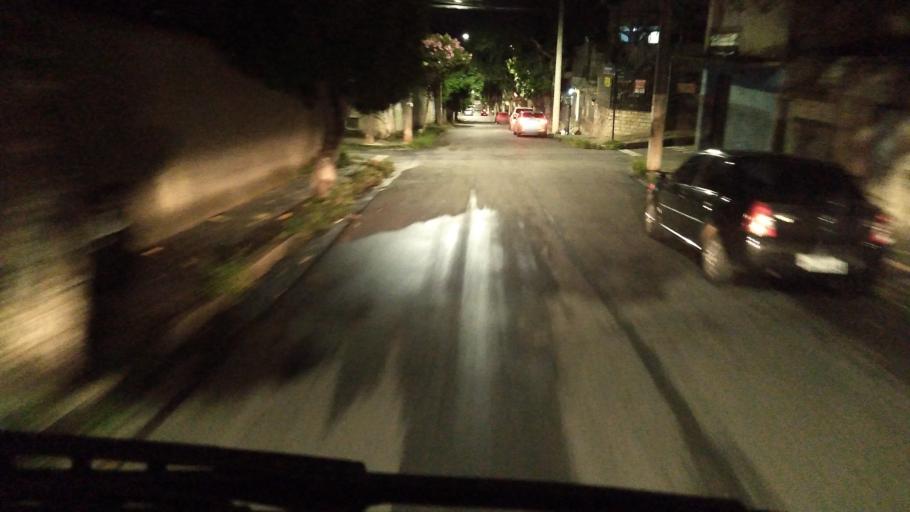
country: BR
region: Minas Gerais
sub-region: Belo Horizonte
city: Belo Horizonte
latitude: -19.8987
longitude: -43.9162
